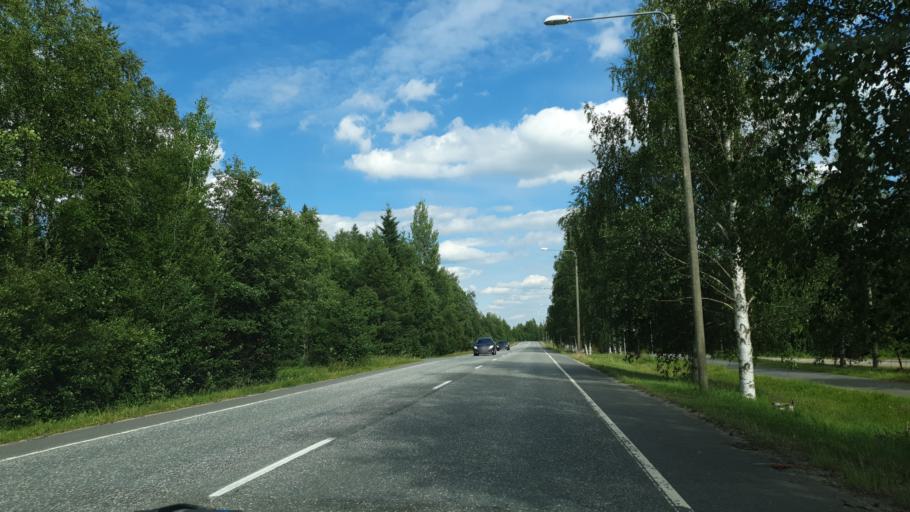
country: FI
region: Kainuu
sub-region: Kajaani
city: Kajaani
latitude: 64.2558
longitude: 27.8101
